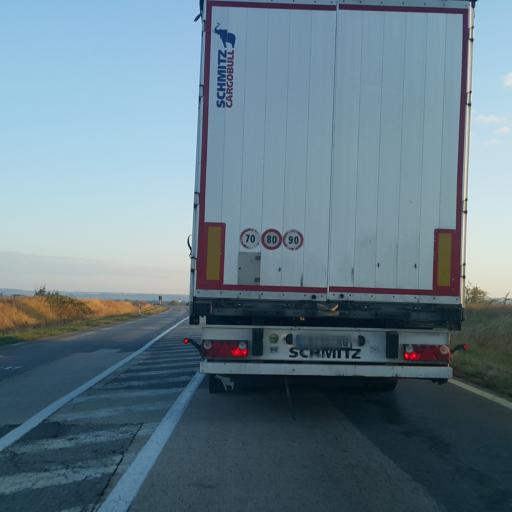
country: RS
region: Central Serbia
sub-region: Zajecarski Okrug
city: Zajecar
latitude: 44.0661
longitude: 22.3348
